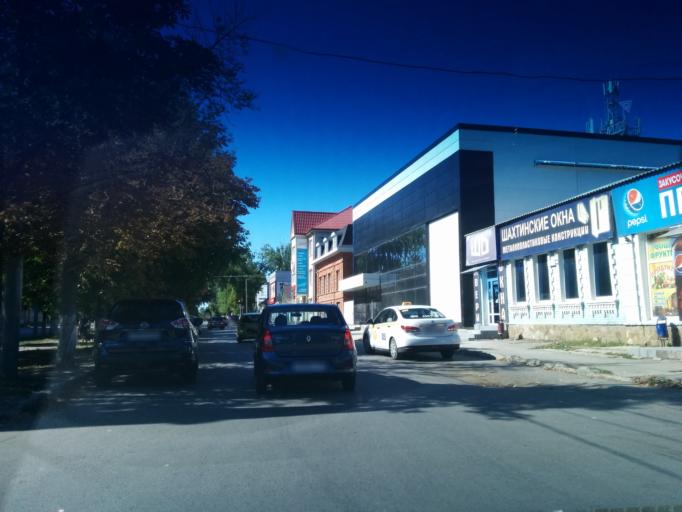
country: RU
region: Rostov
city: Shakhty
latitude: 47.7133
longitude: 40.2119
